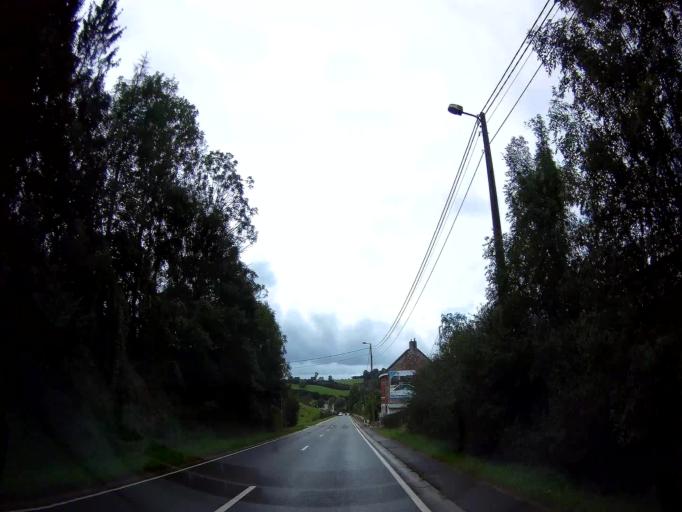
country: BE
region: Wallonia
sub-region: Province de Liege
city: Baelen
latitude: 50.6258
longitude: 5.9648
